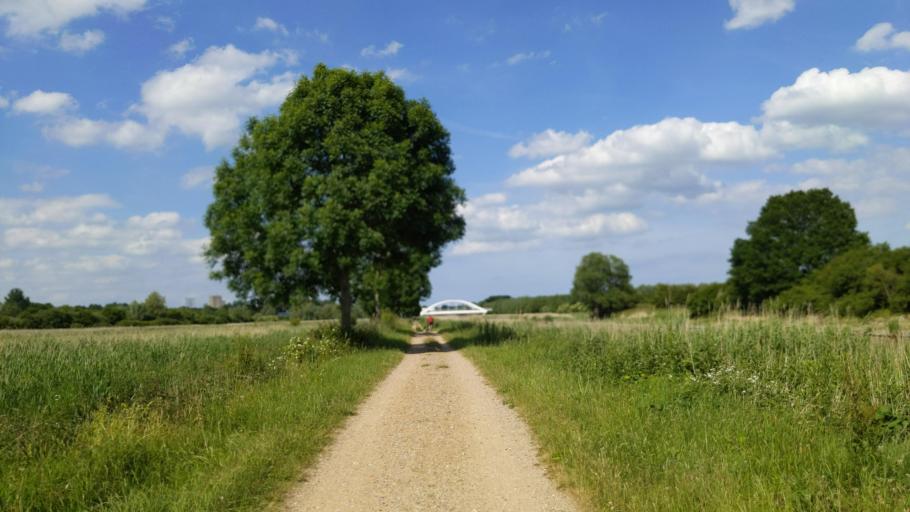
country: DE
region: Schleswig-Holstein
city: Krummesse
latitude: 53.8261
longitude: 10.6356
